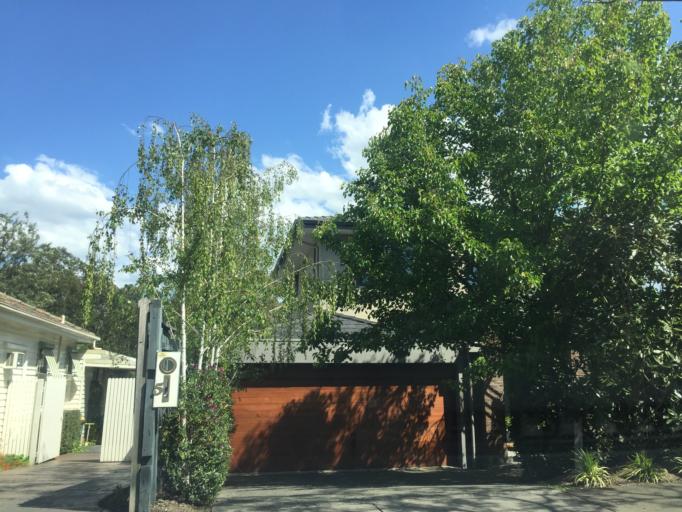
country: AU
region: Victoria
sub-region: Darebin
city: Fairfield
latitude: -37.7843
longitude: 145.0232
